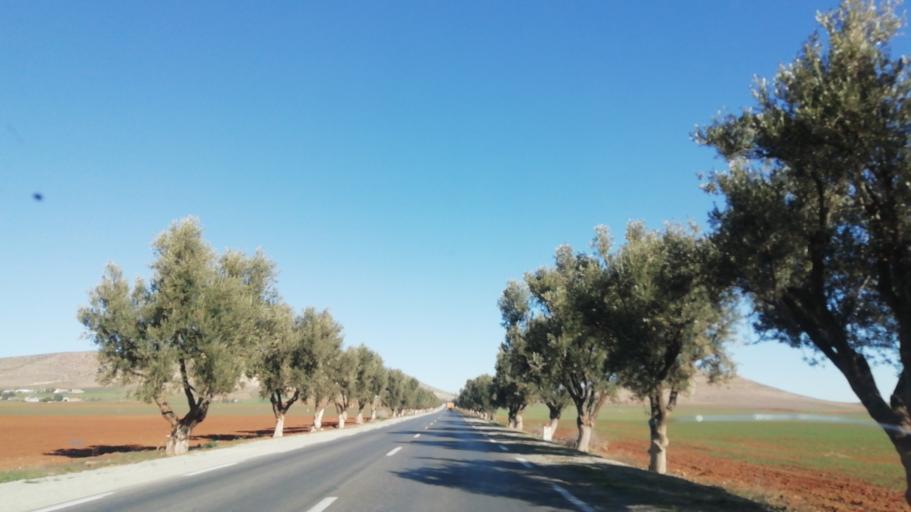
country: DZ
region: Mascara
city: Mascara
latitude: 35.2264
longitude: 0.1145
